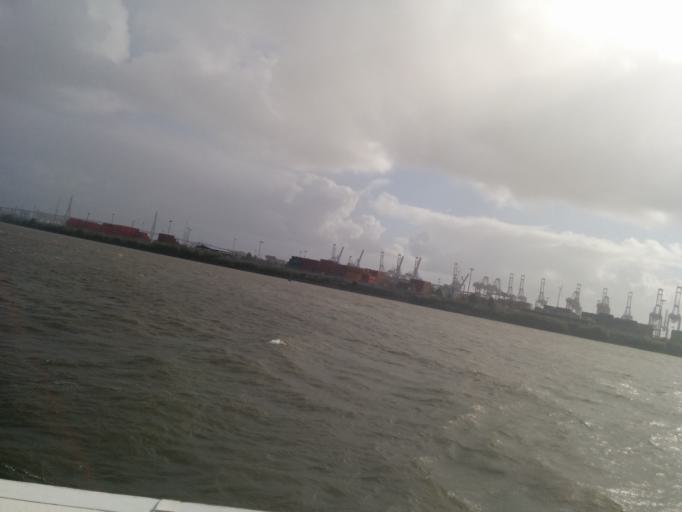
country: DE
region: Hamburg
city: Altona
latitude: 53.5423
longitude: 9.9291
